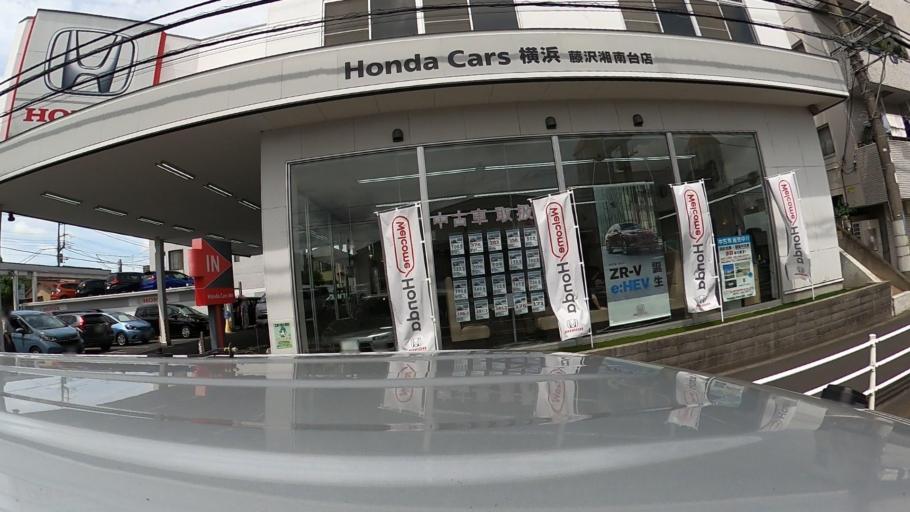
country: JP
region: Kanagawa
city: Fujisawa
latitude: 35.4028
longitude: 139.4695
